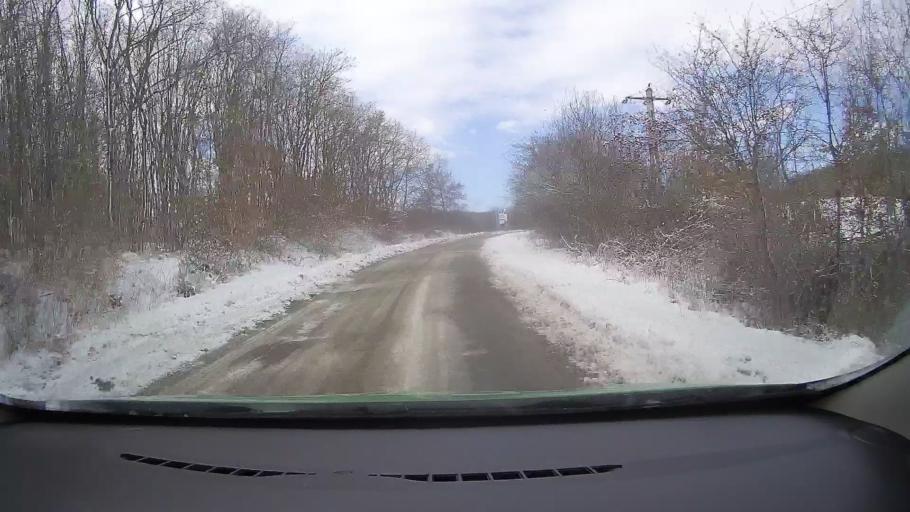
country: RO
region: Sibiu
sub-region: Comuna Altina
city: Altina
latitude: 45.9934
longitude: 24.4298
